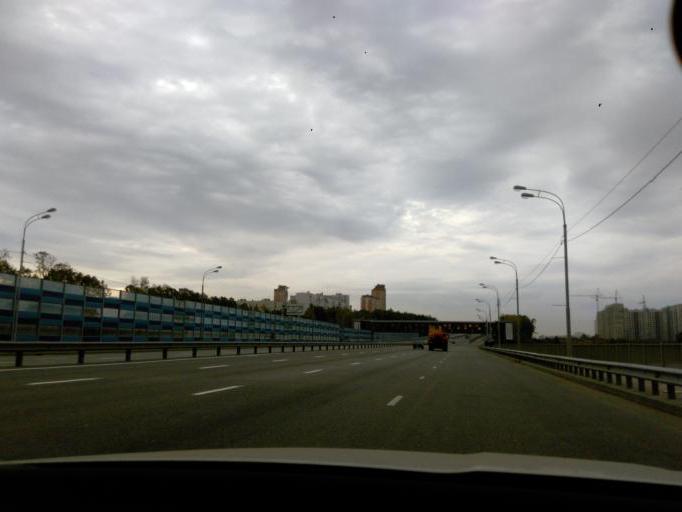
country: RU
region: Moscow
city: Severnyy
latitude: 55.9390
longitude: 37.5446
